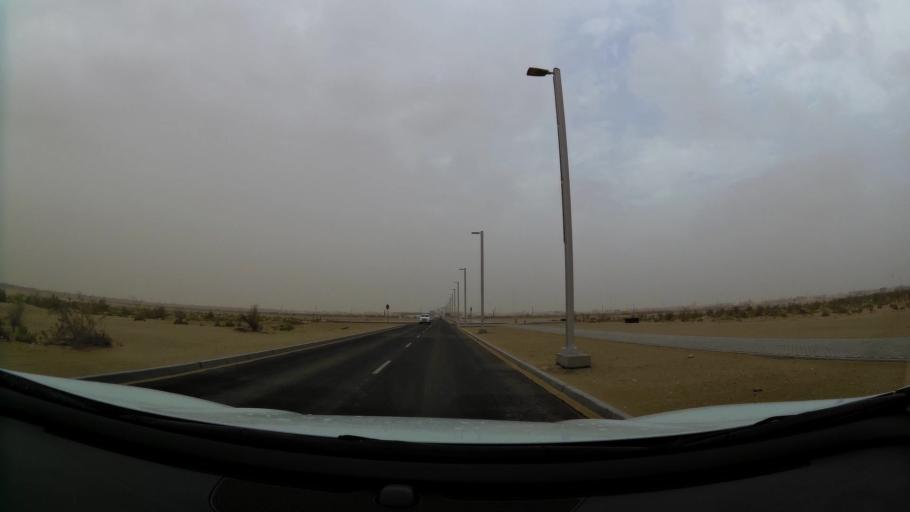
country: AE
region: Abu Dhabi
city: Abu Dhabi
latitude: 24.4242
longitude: 54.6176
